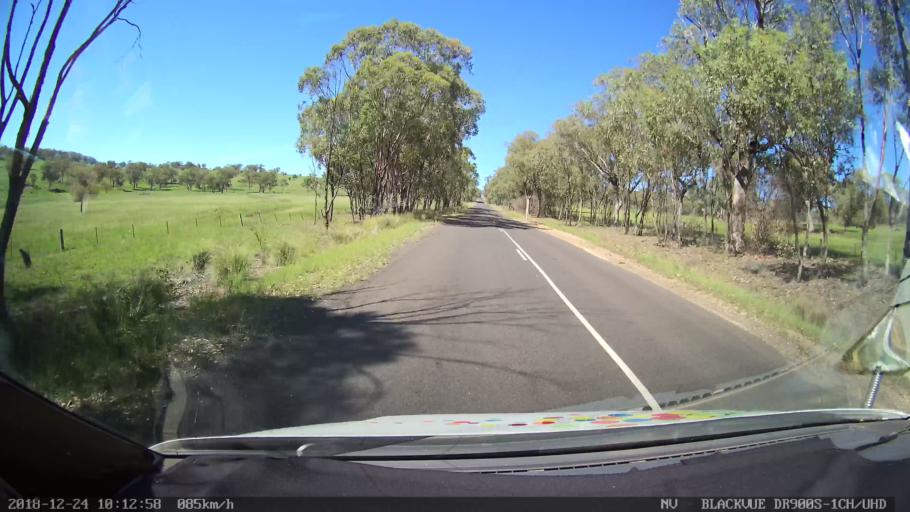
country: AU
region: New South Wales
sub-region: Liverpool Plains
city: Quirindi
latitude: -31.6846
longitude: 150.6433
